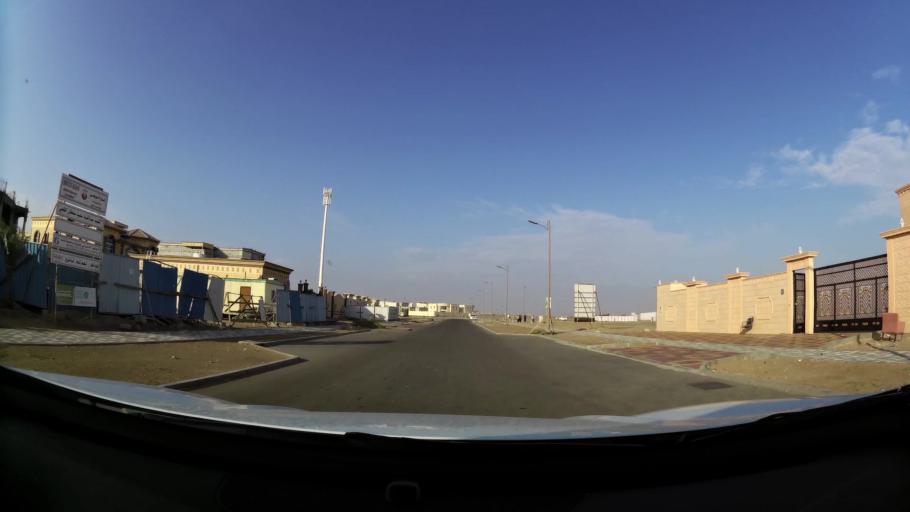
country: AE
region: Abu Dhabi
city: Al Ain
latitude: 24.1091
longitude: 55.8549
